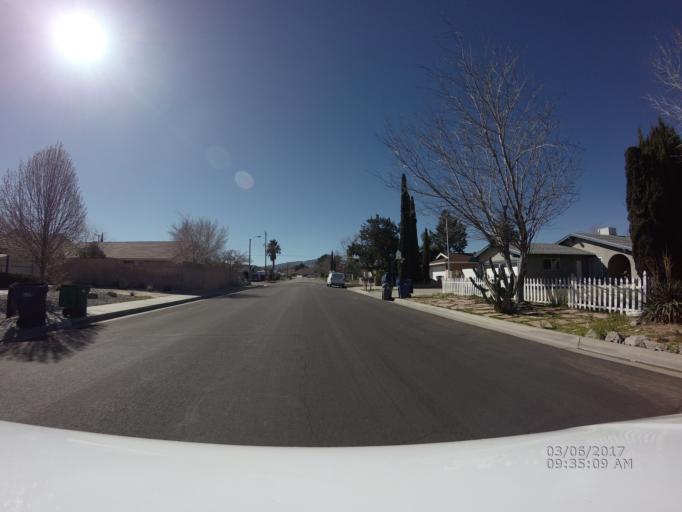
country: US
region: California
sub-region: Los Angeles County
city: Quartz Hill
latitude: 34.6516
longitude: -118.2132
